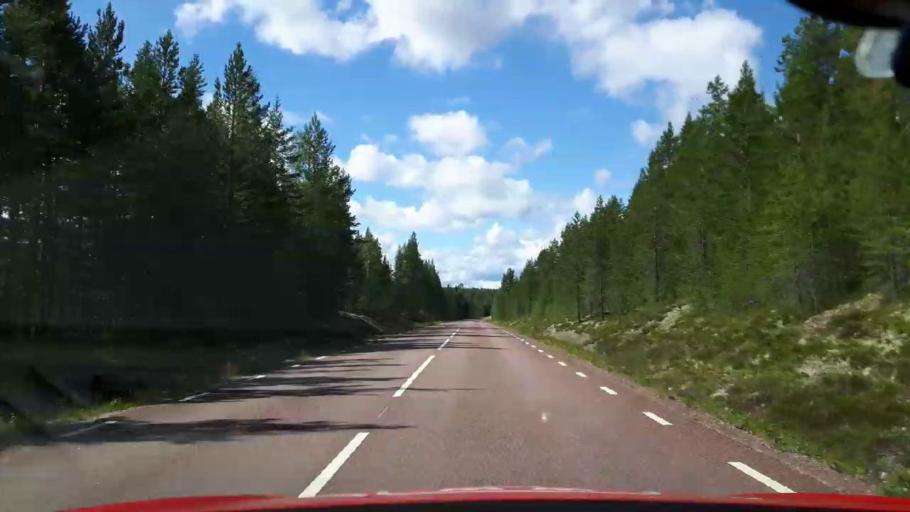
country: SE
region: Jaemtland
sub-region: Harjedalens Kommun
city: Sveg
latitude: 62.0002
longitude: 14.2659
